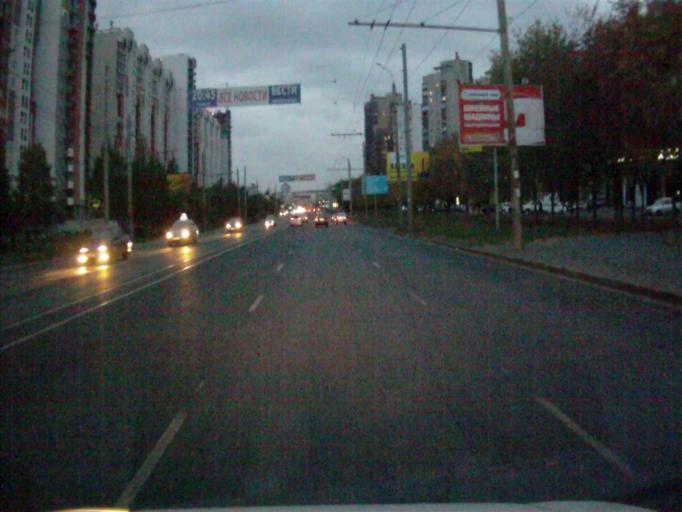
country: RU
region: Chelyabinsk
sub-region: Gorod Chelyabinsk
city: Chelyabinsk
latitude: 55.1762
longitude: 61.3106
